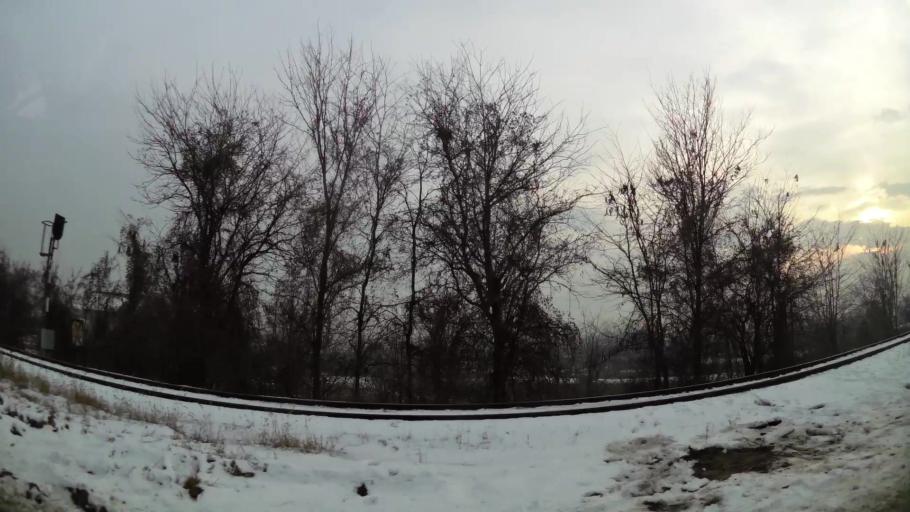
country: MK
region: Suto Orizari
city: Suto Orizare
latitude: 42.0278
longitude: 21.4168
